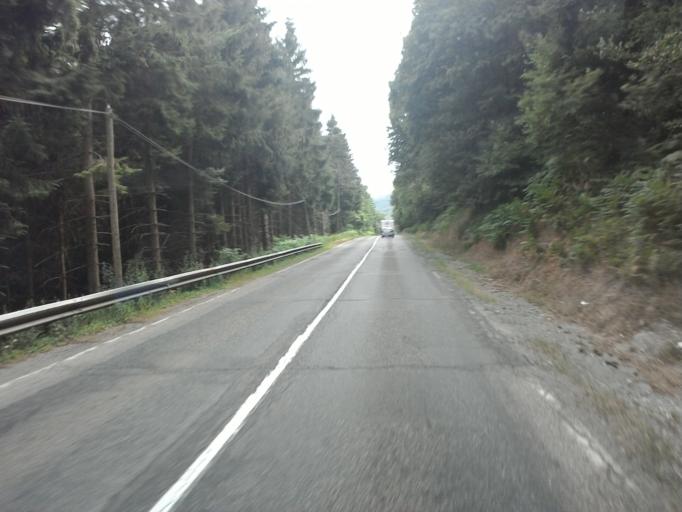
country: FR
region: Rhone-Alpes
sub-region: Departement de l'Isere
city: Pierre-Chatel
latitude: 44.9861
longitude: 5.7732
